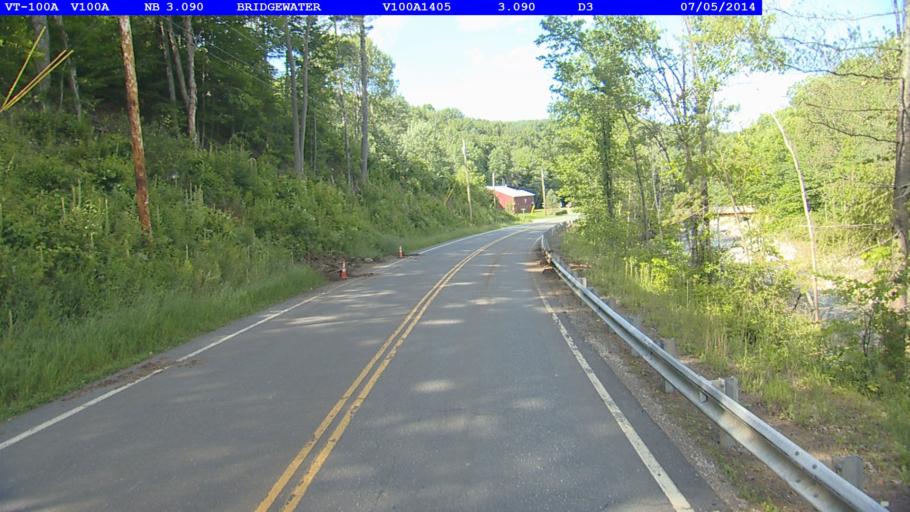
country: US
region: Vermont
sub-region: Windsor County
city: Woodstock
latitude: 43.5586
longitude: -72.7051
